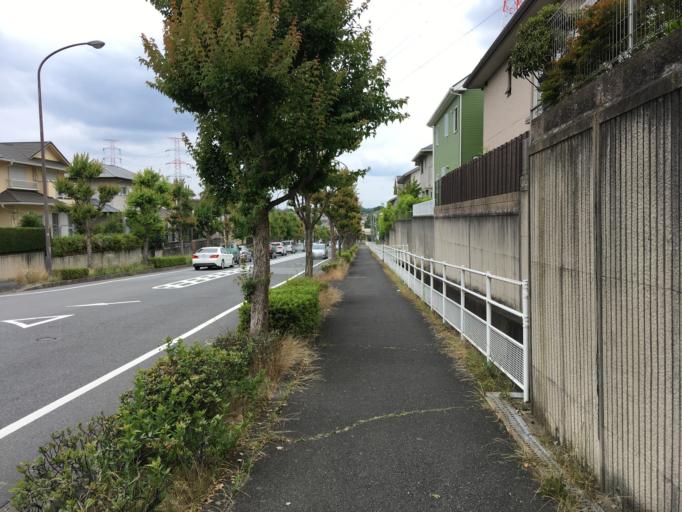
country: JP
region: Nara
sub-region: Ikoma-shi
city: Ikoma
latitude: 34.7240
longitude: 135.7119
